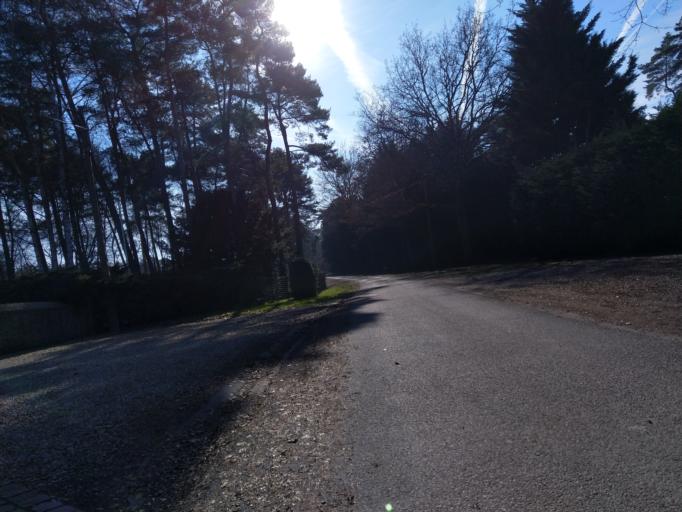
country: BE
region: Wallonia
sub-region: Province du Hainaut
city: Jurbise
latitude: 50.5053
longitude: 3.9277
